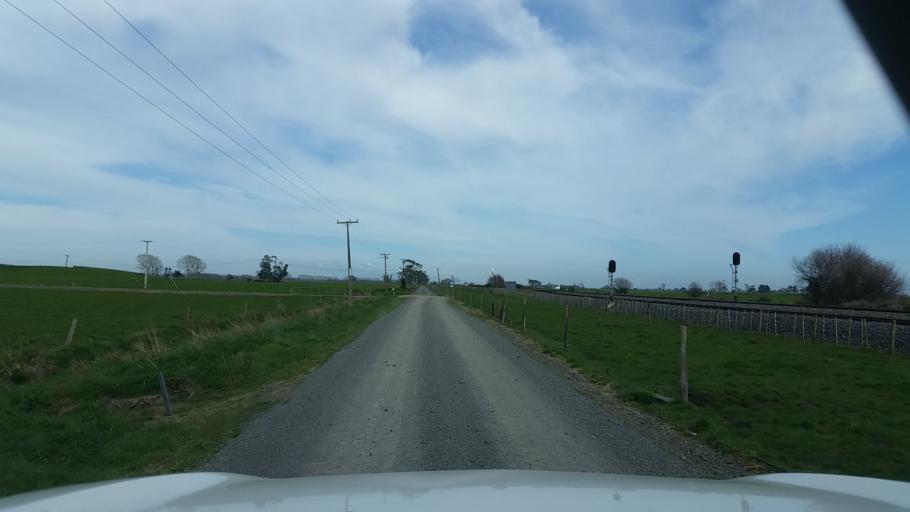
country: NZ
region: Waikato
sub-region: Waipa District
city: Cambridge
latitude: -37.6806
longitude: 175.4576
